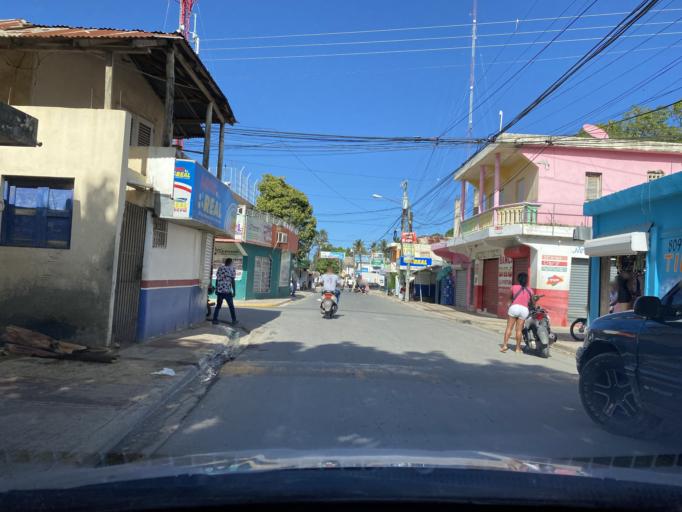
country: DO
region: Samana
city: Las Terrenas
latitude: 19.3130
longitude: -69.5417
